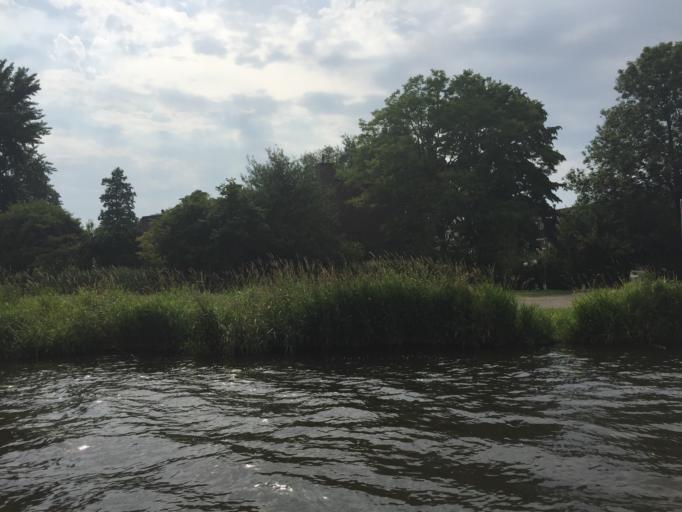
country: NL
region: South Holland
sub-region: Gemeente Leiderdorp
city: Leiderdorp
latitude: 52.1814
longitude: 4.5180
